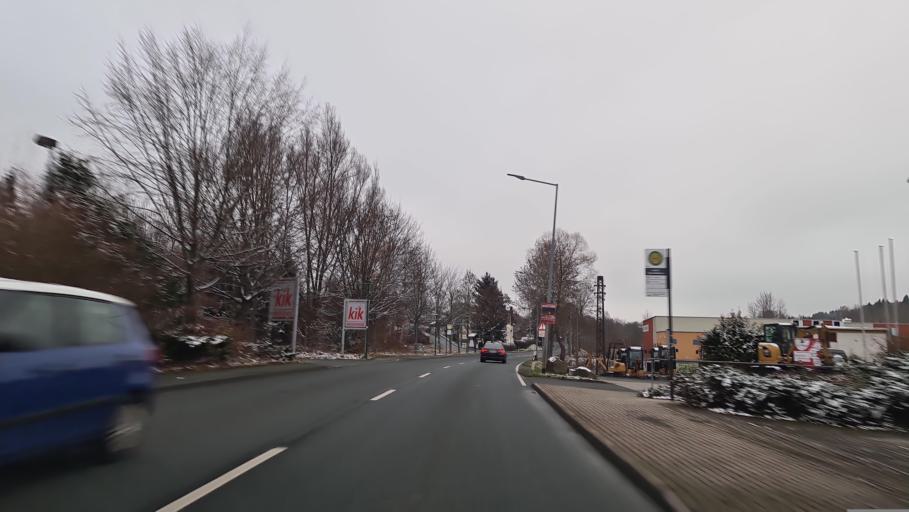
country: DE
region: Saxony
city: Adorf
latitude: 50.3171
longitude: 12.2759
